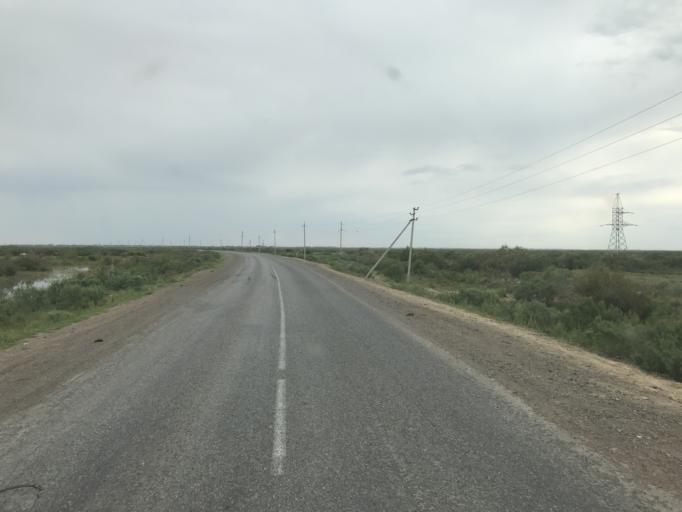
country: KZ
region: Ongtustik Qazaqstan
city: Asykata
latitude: 41.0060
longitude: 68.4746
